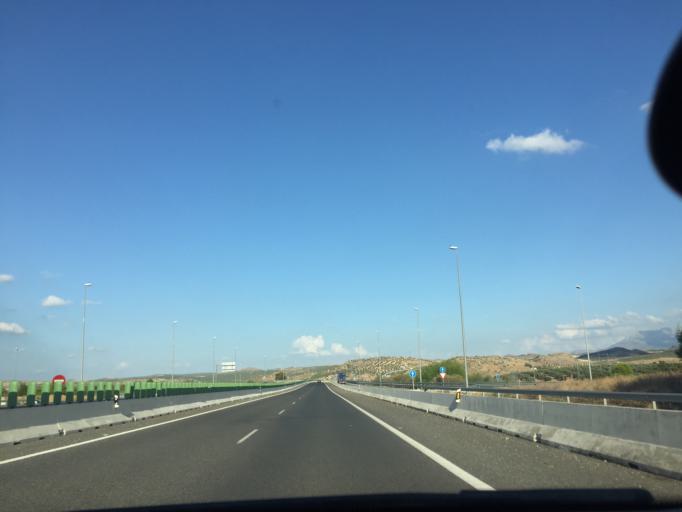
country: ES
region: Andalusia
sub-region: Provincia de Jaen
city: Jaen
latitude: 37.8165
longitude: -3.7687
